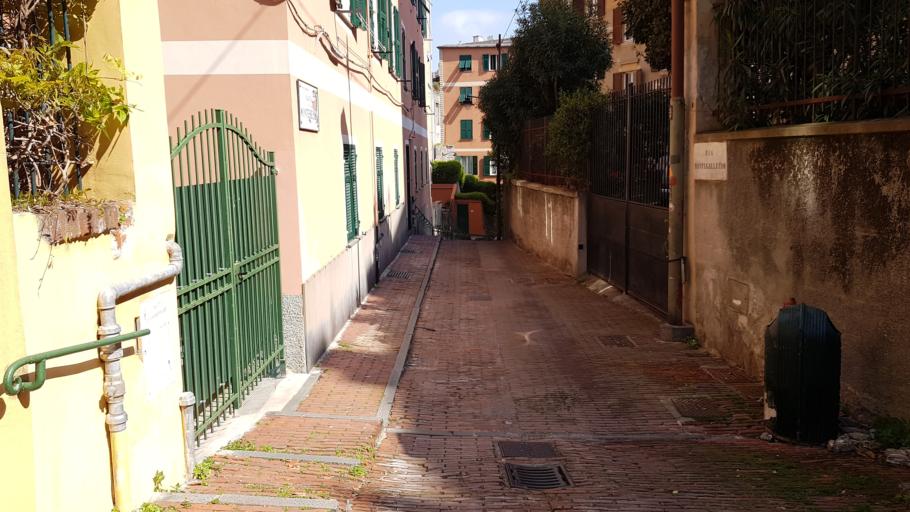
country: IT
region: Liguria
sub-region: Provincia di Genova
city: Genoa
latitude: 44.4174
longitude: 8.9253
